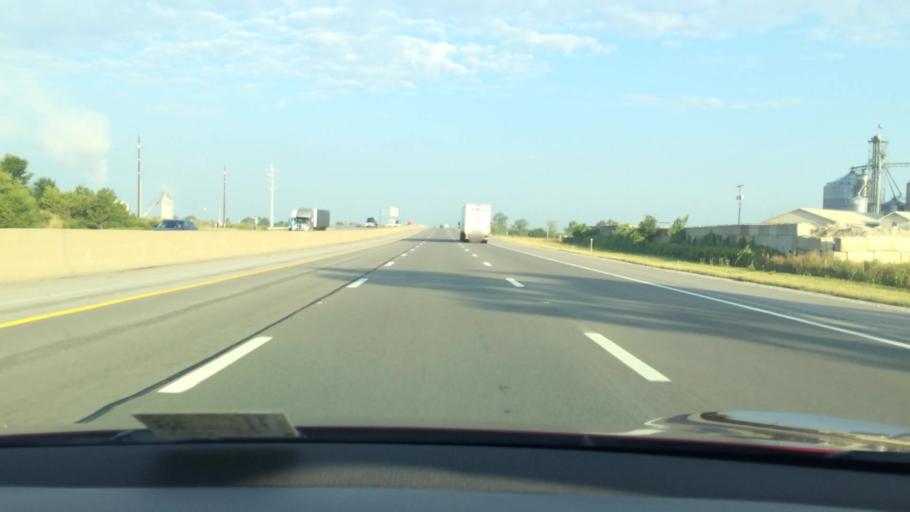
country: US
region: Ohio
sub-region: Huron County
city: Bellevue
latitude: 41.3434
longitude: -82.7788
